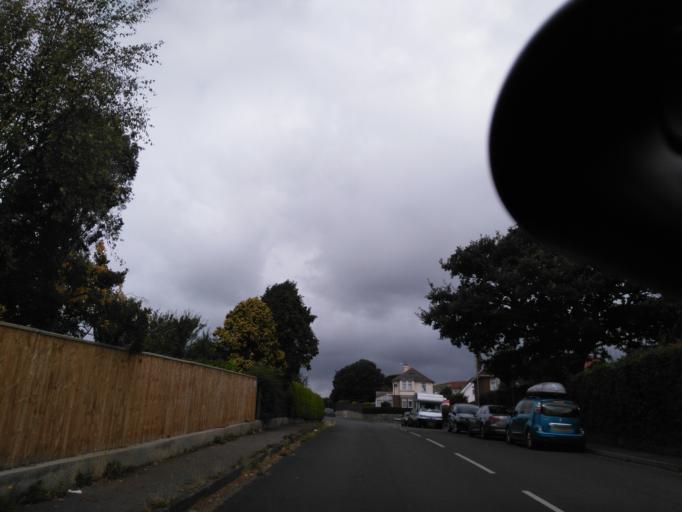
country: GB
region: England
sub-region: Dorset
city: Swanage
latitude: 50.6174
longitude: -1.9624
